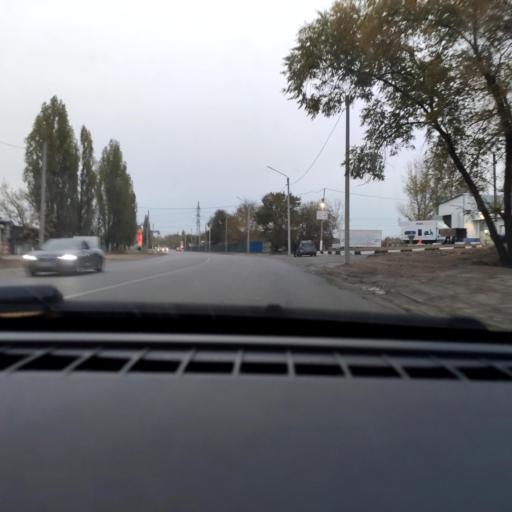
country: RU
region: Voronezj
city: Maslovka
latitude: 51.6256
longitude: 39.2615
